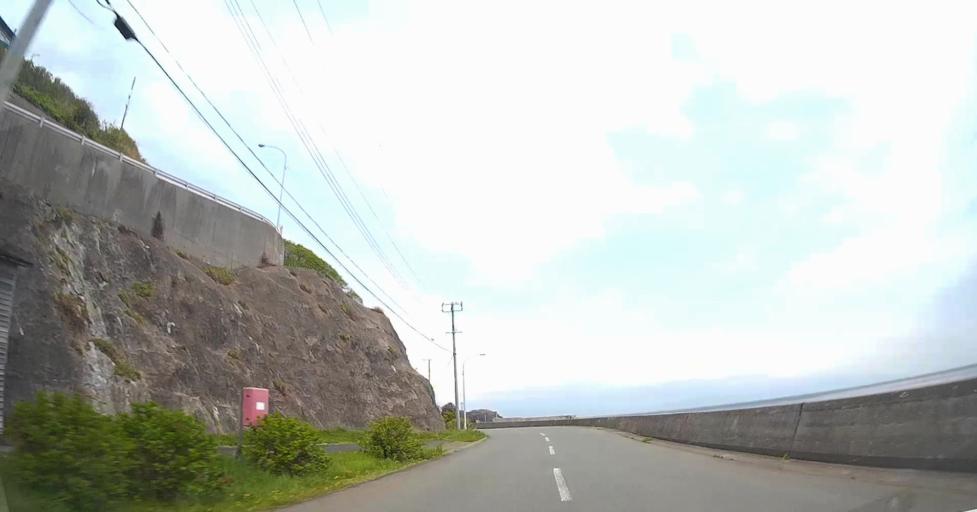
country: JP
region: Aomori
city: Shimokizukuri
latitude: 41.2556
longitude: 140.3518
